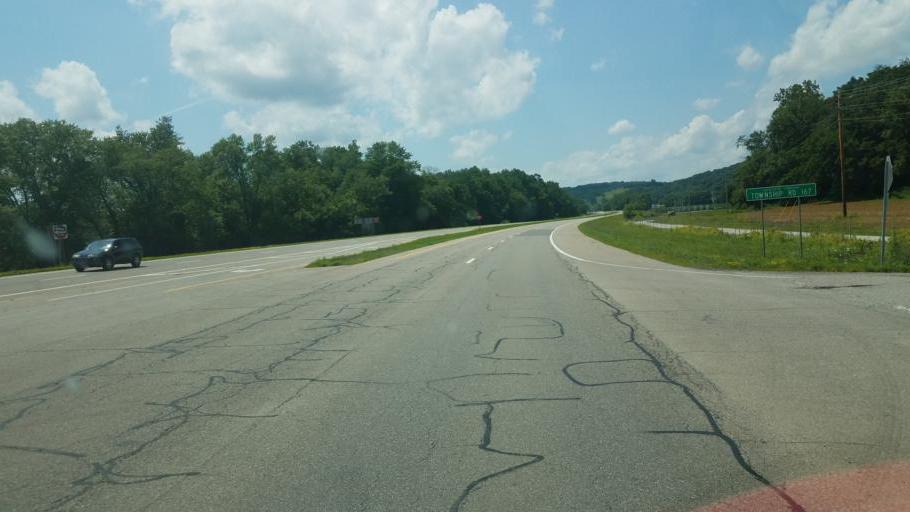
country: US
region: Ohio
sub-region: Coshocton County
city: West Lafayette
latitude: 40.2897
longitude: -81.7362
